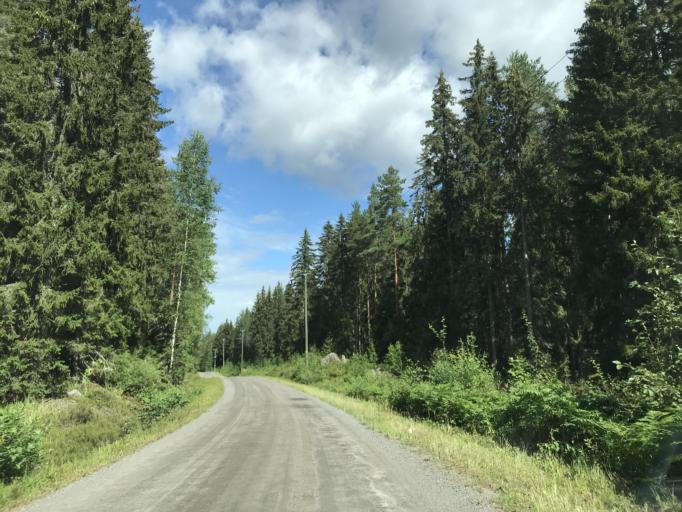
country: FI
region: Uusimaa
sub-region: Helsinki
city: Kaerkoelae
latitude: 60.6276
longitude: 23.7734
